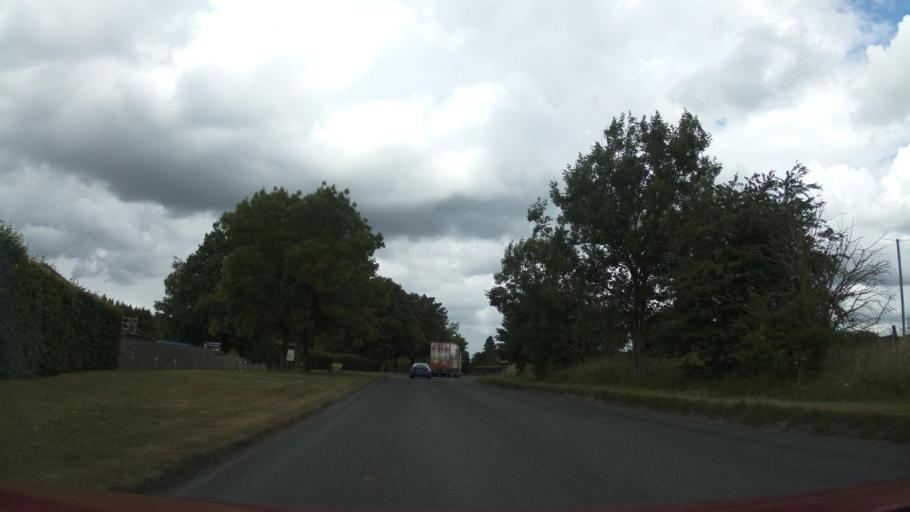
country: GB
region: England
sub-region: Wiltshire
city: Royal Wootton Bassett
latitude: 51.5553
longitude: -1.8989
